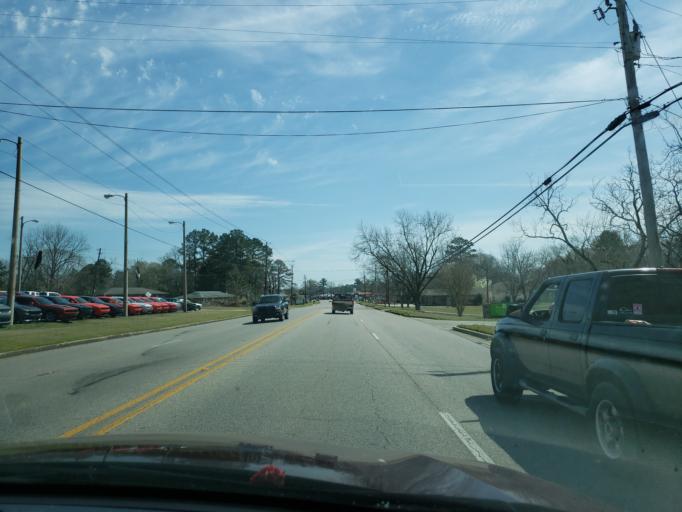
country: US
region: Alabama
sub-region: Elmore County
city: Tallassee
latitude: 32.5569
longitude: -85.9261
